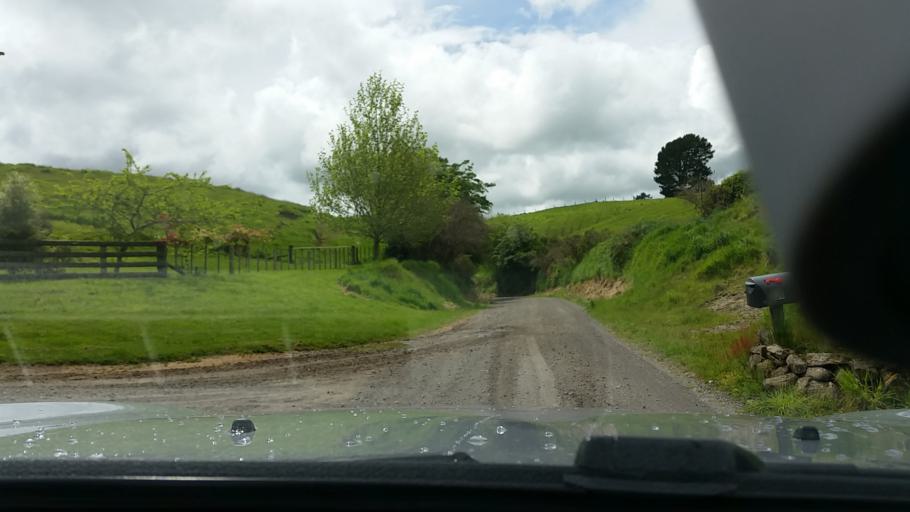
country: NZ
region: Waikato
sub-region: Taupo District
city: Taupo
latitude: -38.4337
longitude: 176.1587
